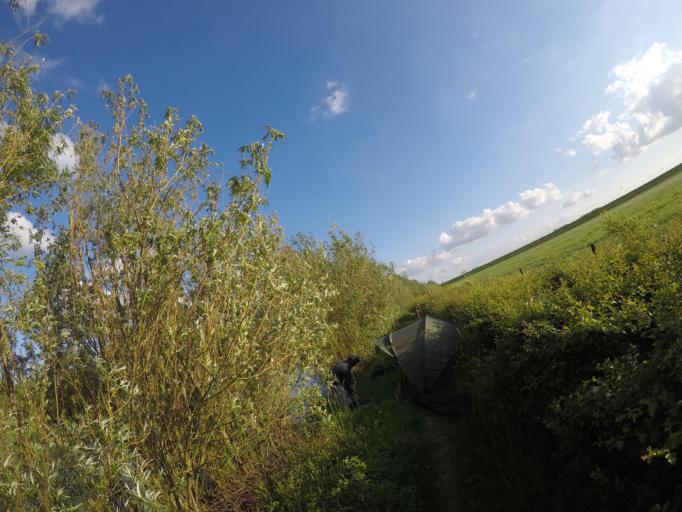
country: NL
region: Gelderland
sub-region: Gemeente Westervoort
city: Westervoort
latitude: 51.9525
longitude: 5.9634
